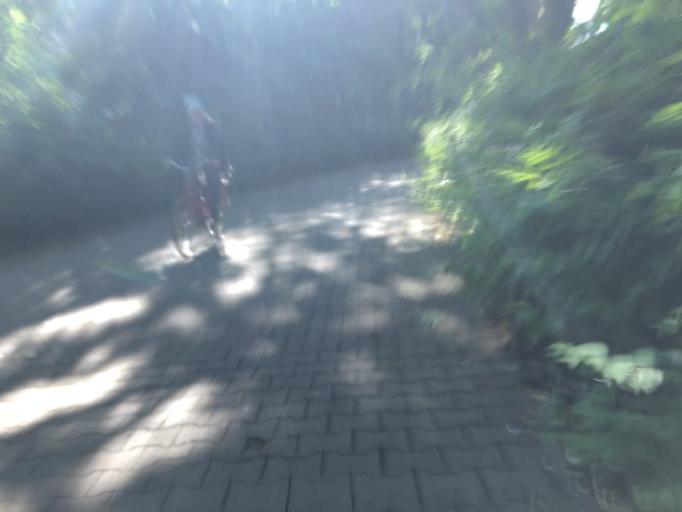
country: DE
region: Bavaria
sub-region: Regierungsbezirk Mittelfranken
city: Erlangen
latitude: 49.5860
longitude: 10.9876
